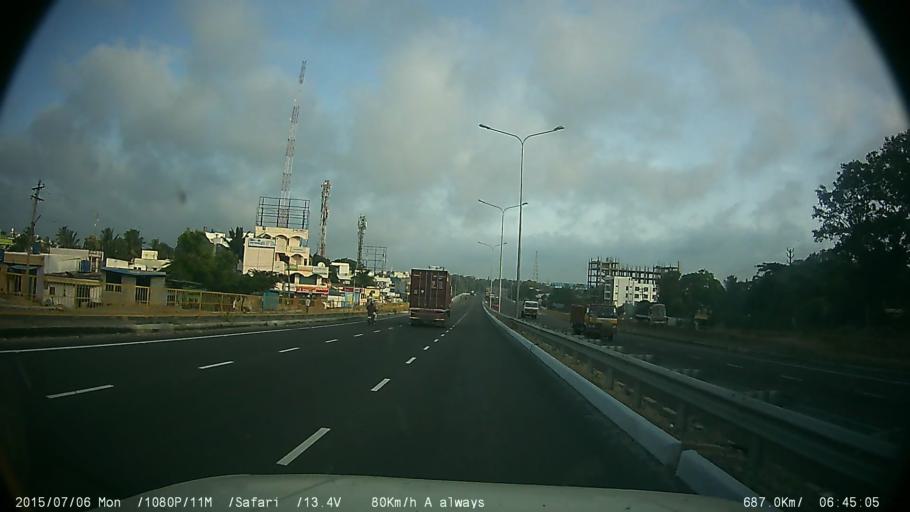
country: IN
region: Tamil Nadu
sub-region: Krishnagiri
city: Hosur
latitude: 12.7503
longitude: 77.8053
